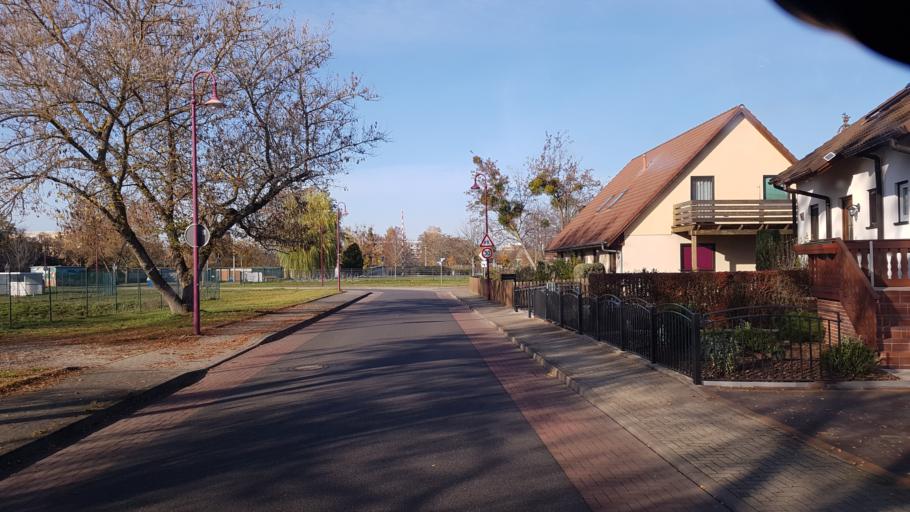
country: DE
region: Brandenburg
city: Grossraschen
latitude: 51.5912
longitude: 14.0067
